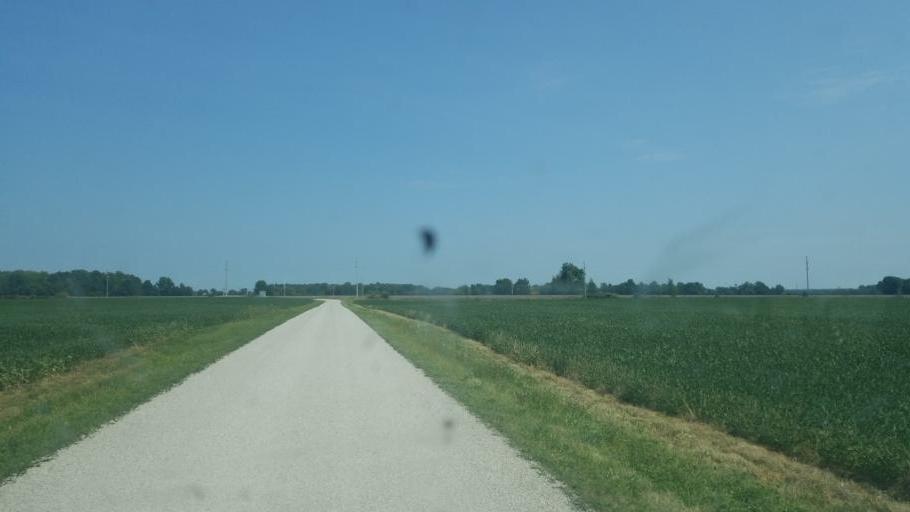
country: US
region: Ohio
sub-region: Crawford County
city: Crestline
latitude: 40.8252
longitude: -82.7103
